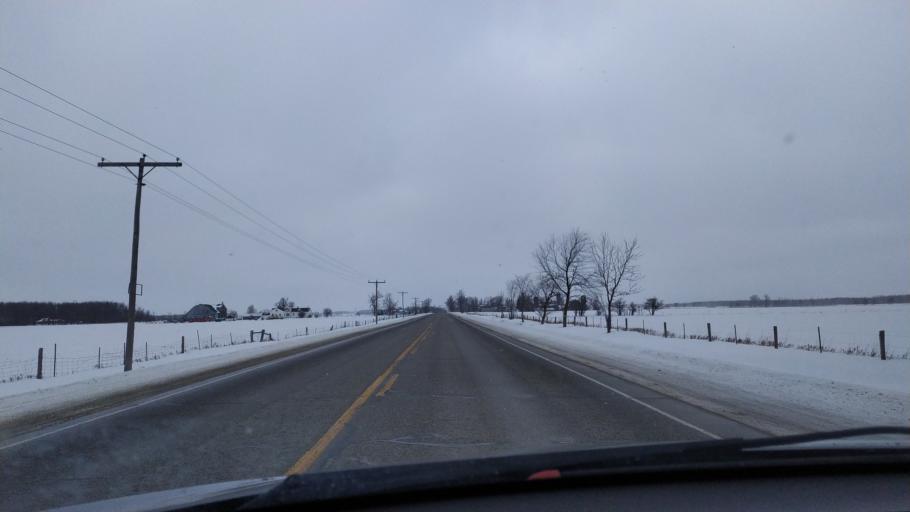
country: CA
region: Ontario
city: North Perth
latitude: 43.5779
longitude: -80.8497
